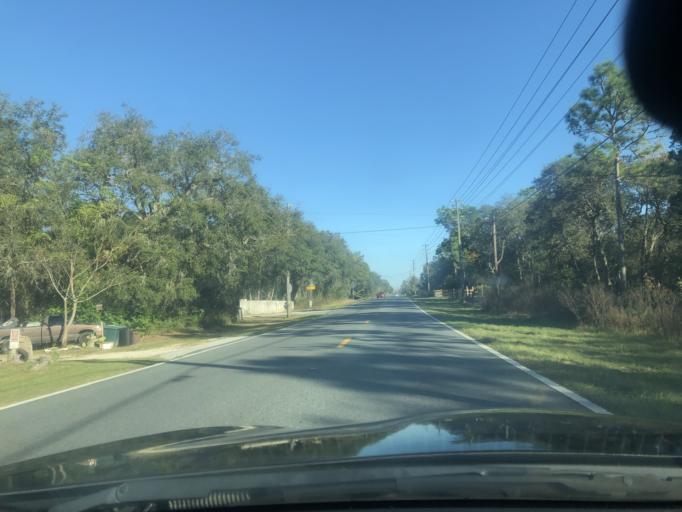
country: US
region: Florida
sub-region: Citrus County
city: Sugarmill Woods
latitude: 28.7640
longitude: -82.5436
